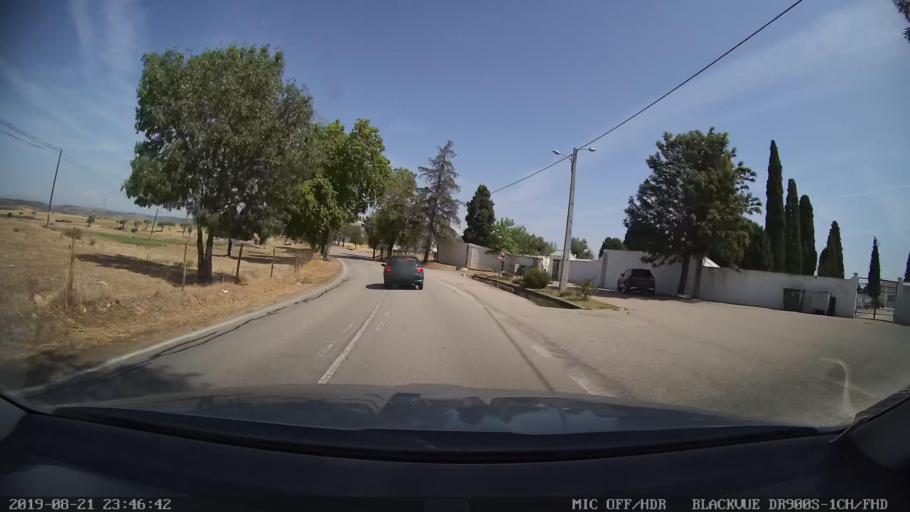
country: PT
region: Castelo Branco
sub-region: Idanha-A-Nova
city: Idanha-a-Nova
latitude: 39.8439
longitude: -7.2564
